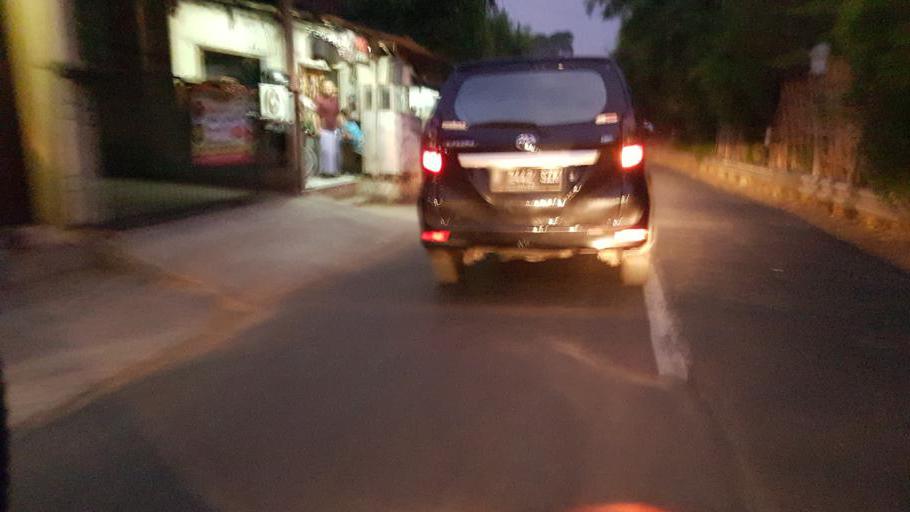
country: ID
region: Jakarta Raya
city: Jakarta
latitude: -6.3015
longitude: 106.8263
